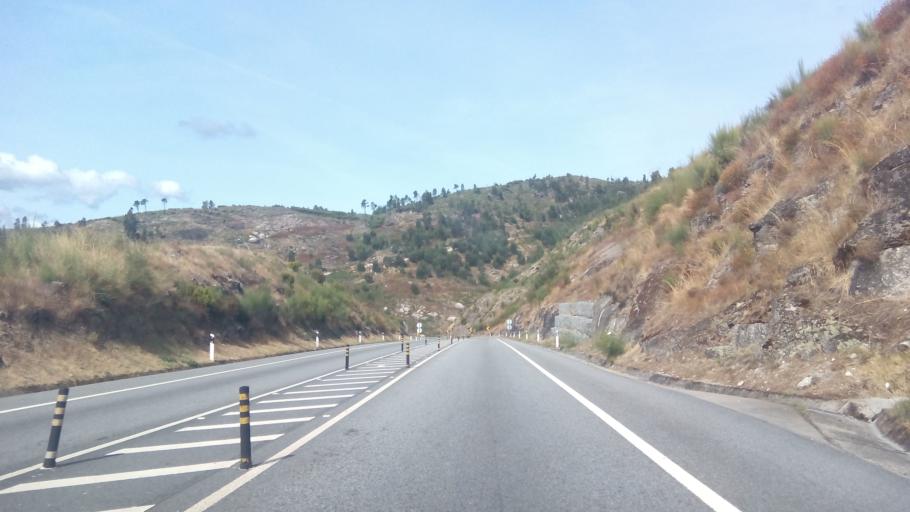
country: PT
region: Porto
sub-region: Amarante
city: Amarante
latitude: 41.2657
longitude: -7.9793
